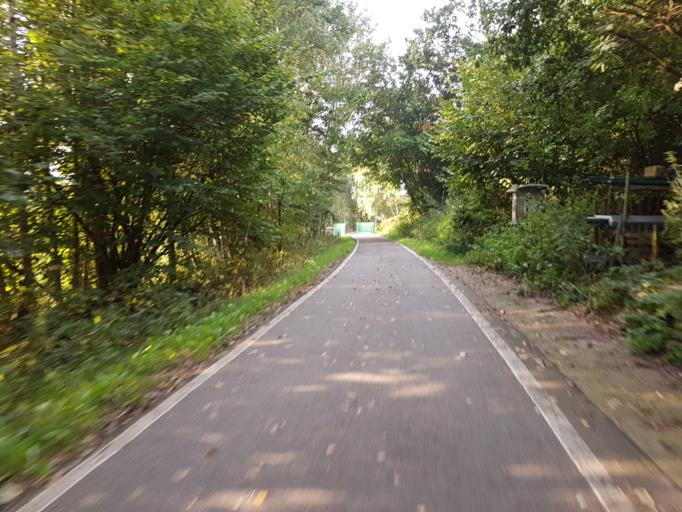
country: DE
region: Saxony
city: Wittgensdorf
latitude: 50.8896
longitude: 12.8904
